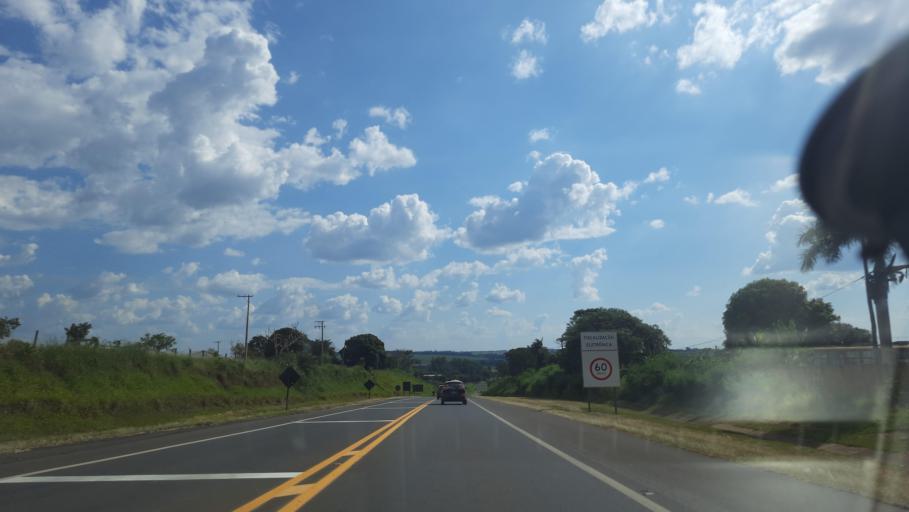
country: BR
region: Sao Paulo
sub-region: Casa Branca
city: Casa Branca
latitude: -21.7374
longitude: -46.9738
